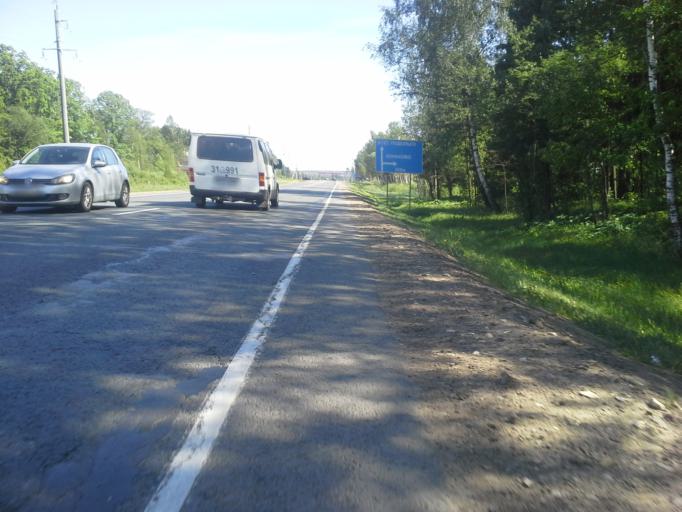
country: RU
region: Moskovskaya
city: Troitsk
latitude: 55.4259
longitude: 37.1747
